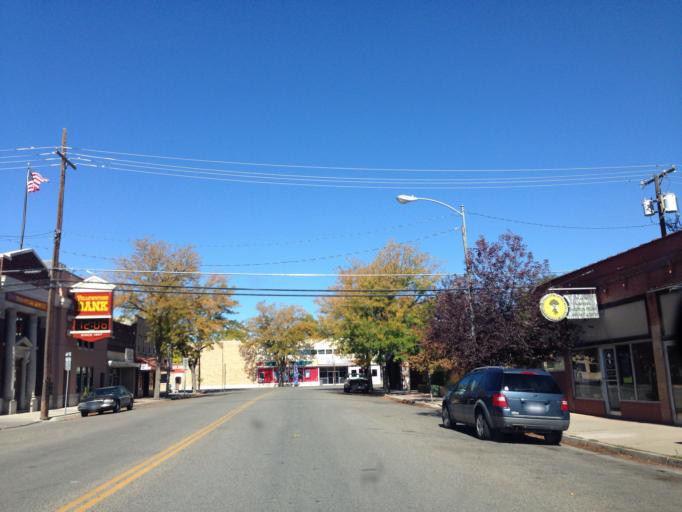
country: US
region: Montana
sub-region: Yellowstone County
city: Laurel
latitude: 45.6695
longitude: -108.7715
